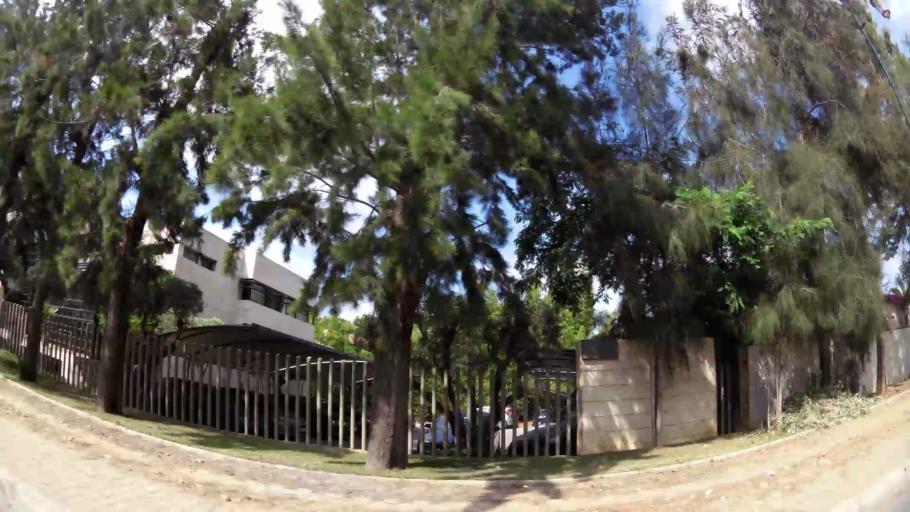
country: MA
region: Rabat-Sale-Zemmour-Zaer
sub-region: Rabat
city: Rabat
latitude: 33.9813
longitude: -6.8445
